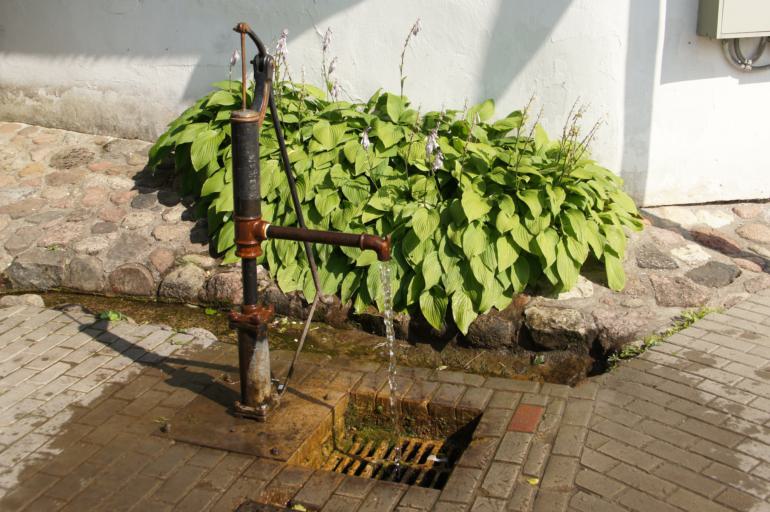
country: LV
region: Talsu Rajons
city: Sabile
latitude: 57.0461
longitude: 22.5727
